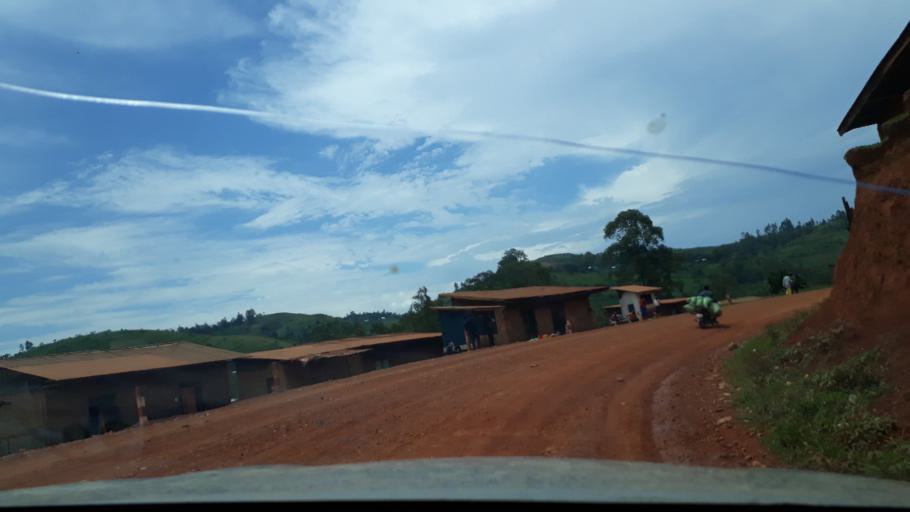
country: CD
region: Eastern Province
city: Bunia
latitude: 1.7319
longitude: 30.3014
